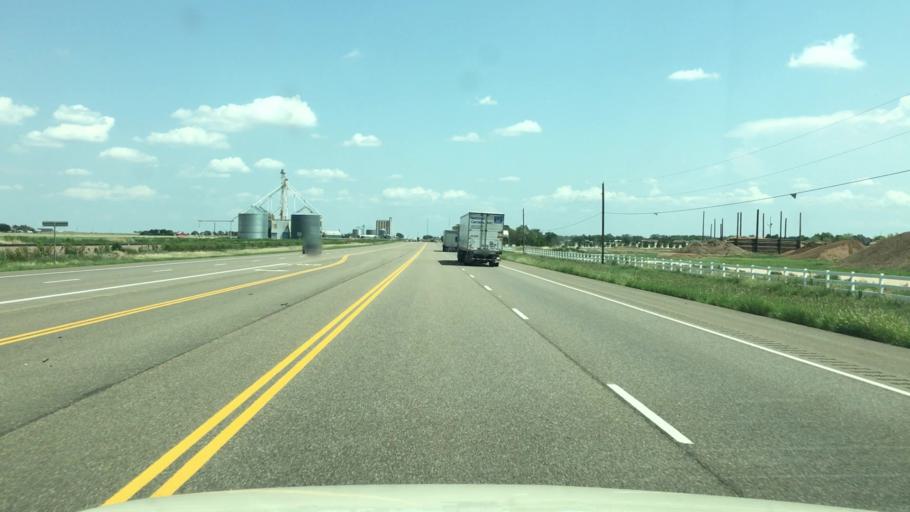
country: US
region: Texas
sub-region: Armstrong County
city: Claude
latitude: 35.1189
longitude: -101.3800
